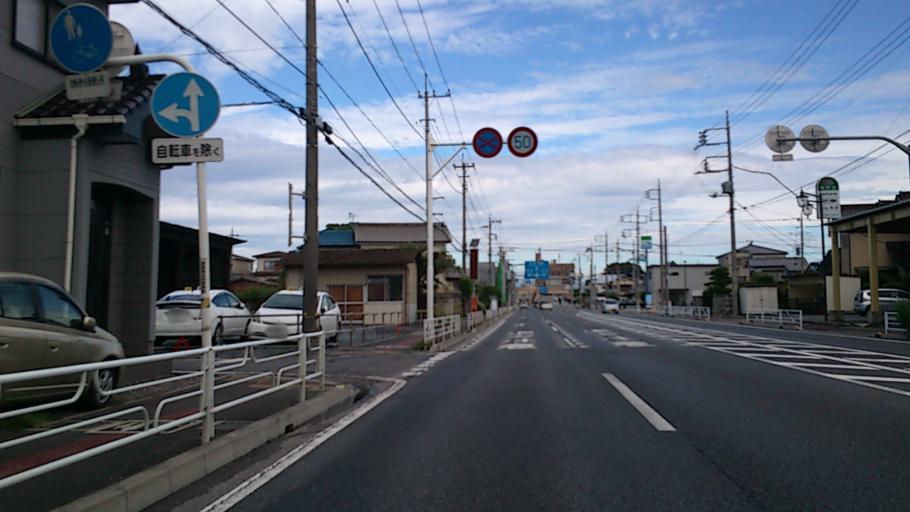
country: JP
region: Gunma
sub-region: Sawa-gun
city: Tamamura
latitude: 36.2717
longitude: 139.1106
